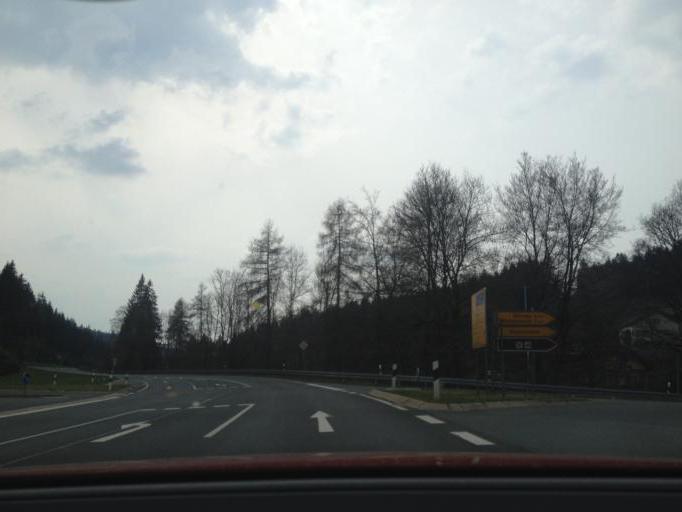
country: DE
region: Bavaria
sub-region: Upper Franconia
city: Bischofsgrun
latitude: 50.0543
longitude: 11.7782
